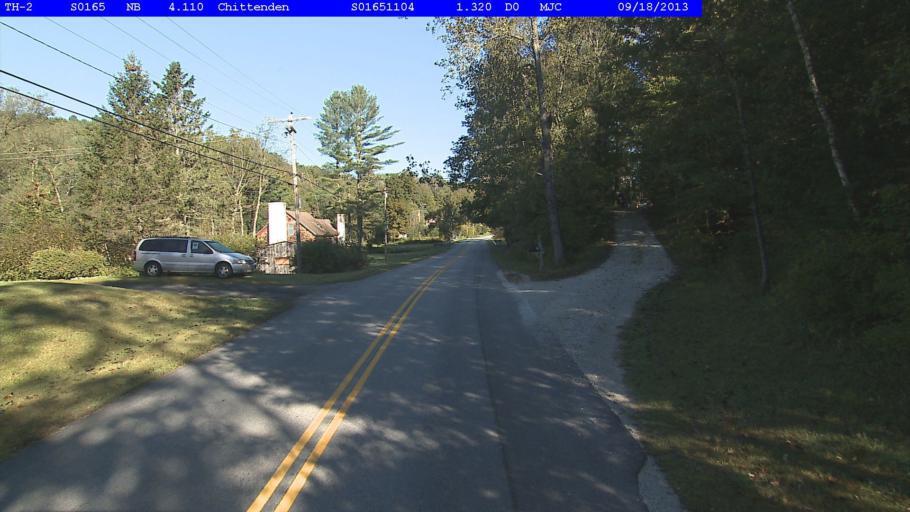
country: US
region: Vermont
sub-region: Rutland County
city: Rutland
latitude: 43.6952
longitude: -72.9561
